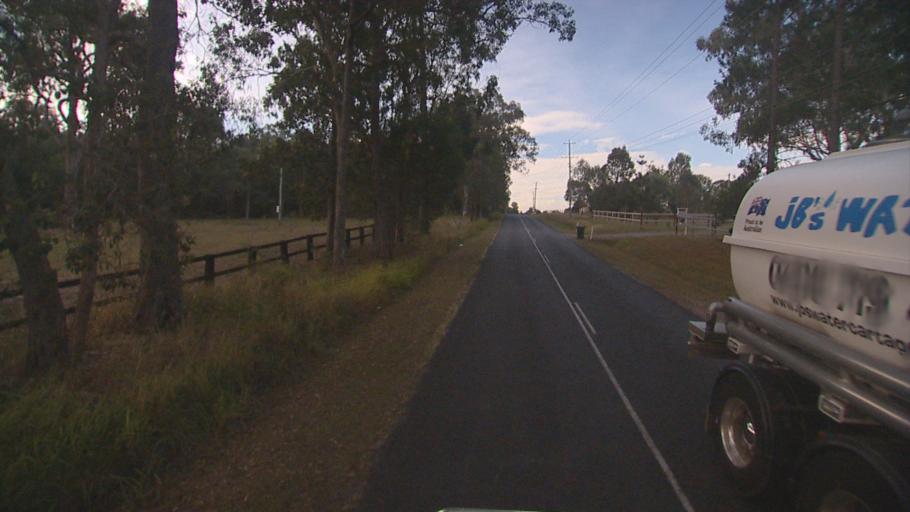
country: AU
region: Queensland
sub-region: Logan
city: Cedar Vale
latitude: -27.8380
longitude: 153.1063
